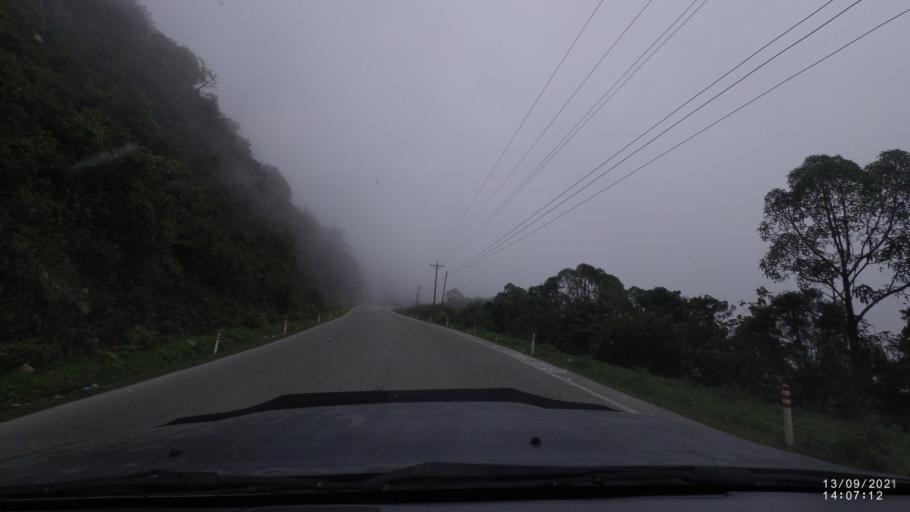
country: BO
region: Cochabamba
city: Colomi
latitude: -17.1817
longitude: -65.8871
